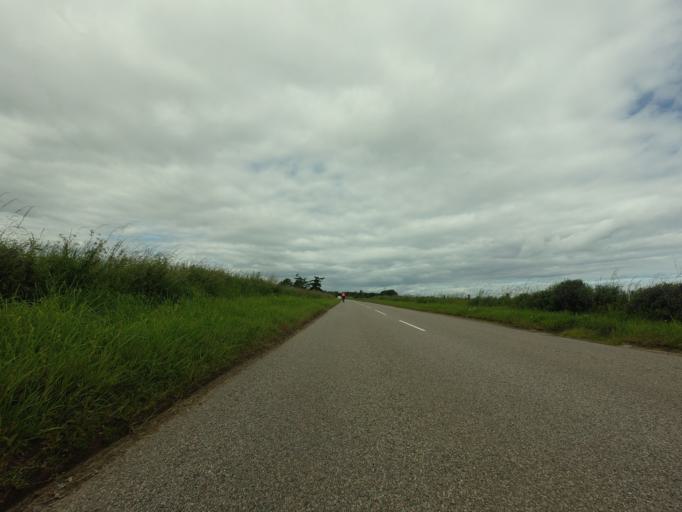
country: GB
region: Scotland
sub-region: Moray
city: Kinloss
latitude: 57.6286
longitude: -3.5493
